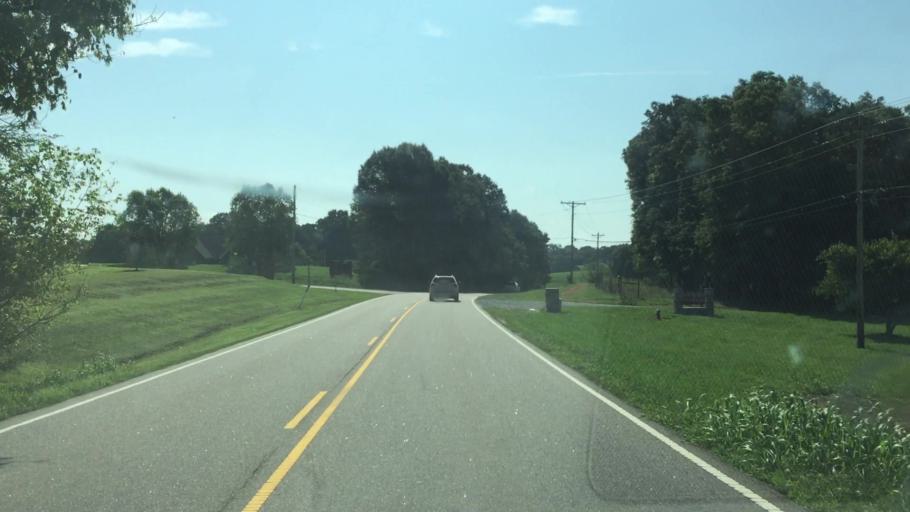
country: US
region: North Carolina
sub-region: Union County
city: Unionville
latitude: 35.1327
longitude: -80.4453
